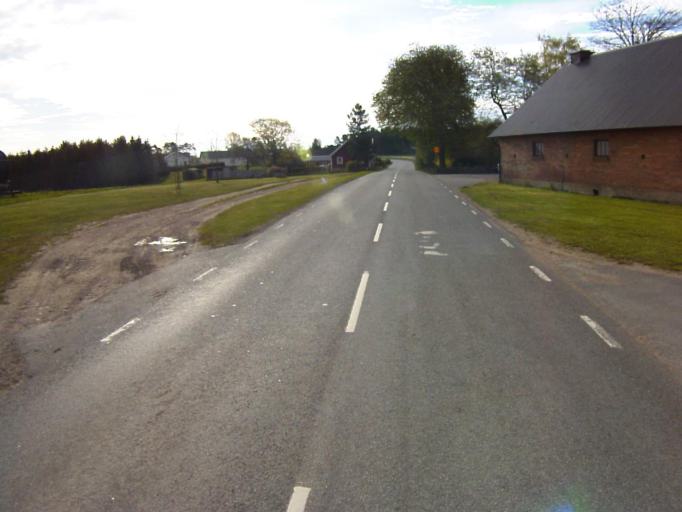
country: SE
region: Skane
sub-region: Kristianstads Kommun
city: Norra Asum
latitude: 55.9923
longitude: 14.1310
